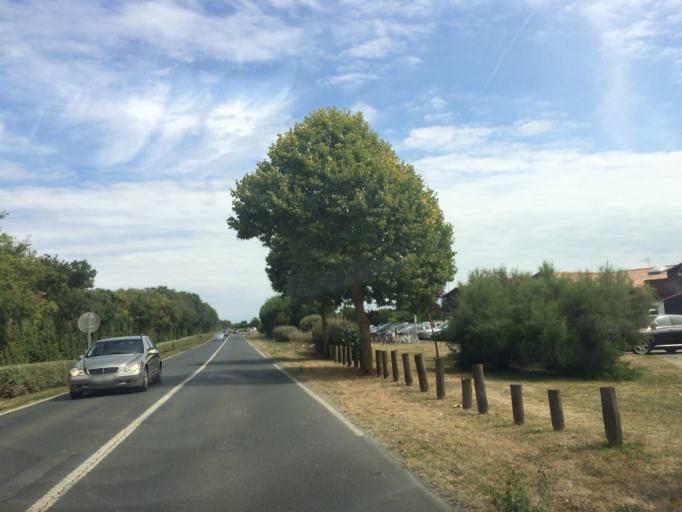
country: FR
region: Poitou-Charentes
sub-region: Departement de la Charente-Maritime
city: Saint-Martin-de-Re
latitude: 46.1970
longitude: -1.3522
